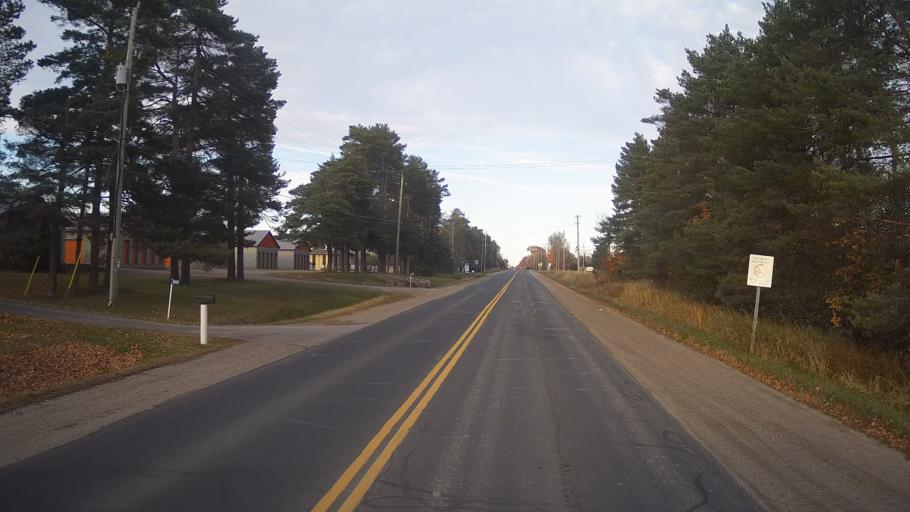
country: CA
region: Ontario
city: Perth
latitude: 44.8864
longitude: -76.2503
